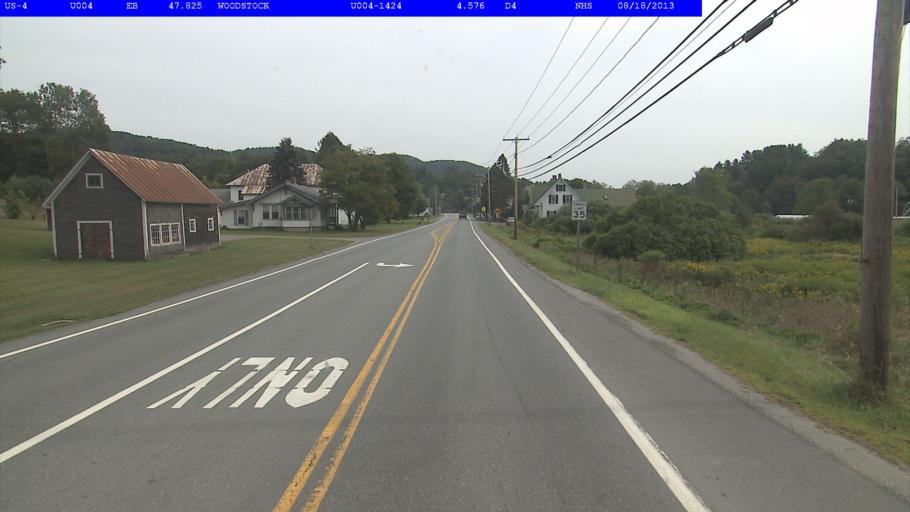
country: US
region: Vermont
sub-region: Windsor County
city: Woodstock
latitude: 43.6139
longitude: -72.5468
